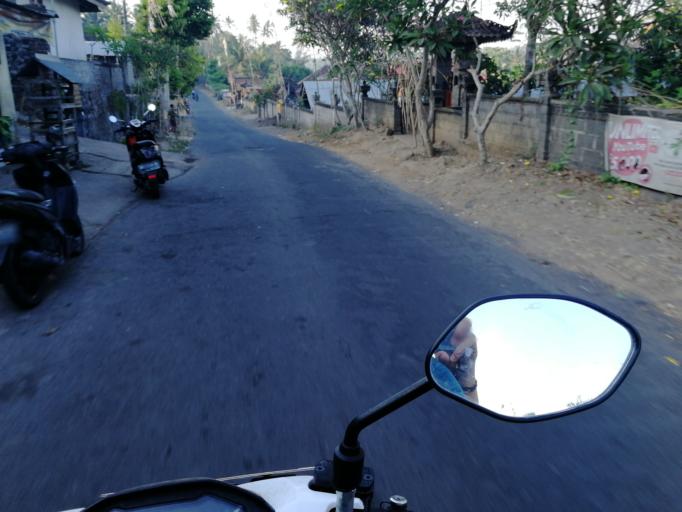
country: ID
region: Bali
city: Tistagede
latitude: -8.3893
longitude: 115.6158
